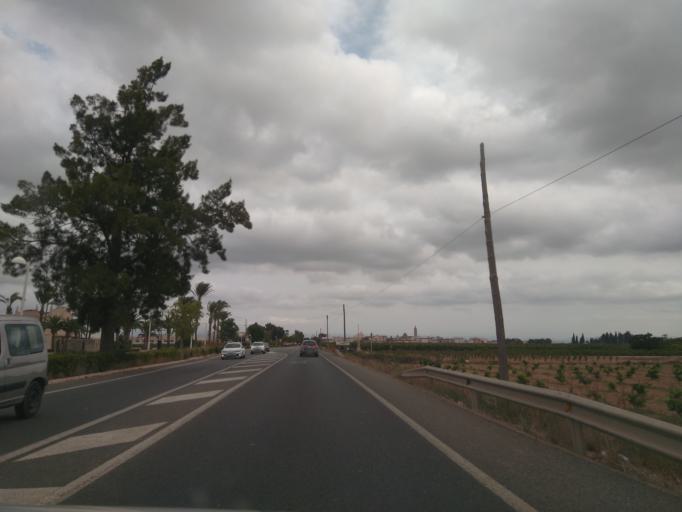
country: ES
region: Valencia
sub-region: Provincia de Valencia
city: L'Alcudia
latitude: 39.2097
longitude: -0.5113
